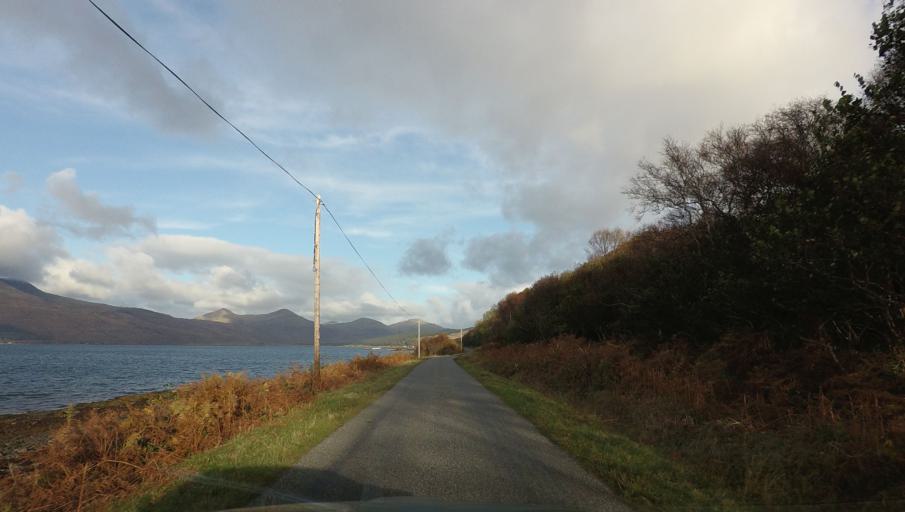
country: GB
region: Scotland
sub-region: Argyll and Bute
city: Isle Of Mull
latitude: 56.3579
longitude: -6.0554
